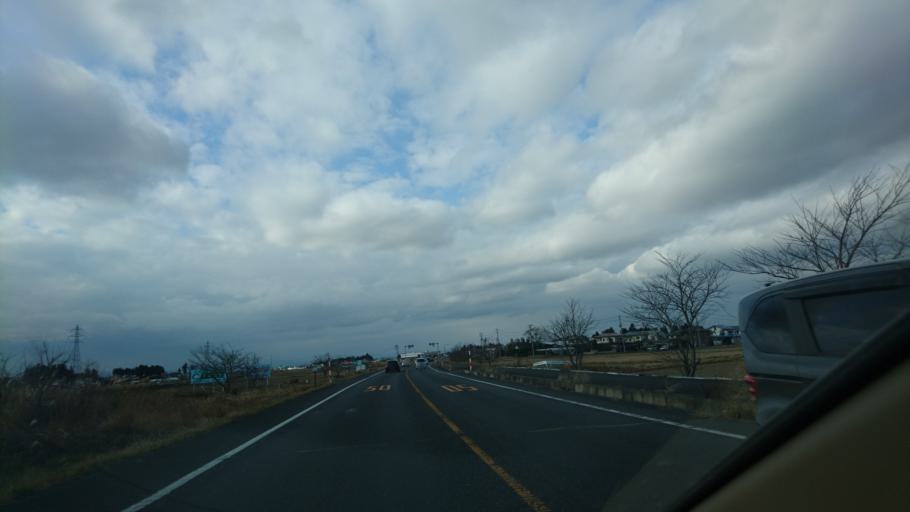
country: JP
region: Miyagi
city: Kogota
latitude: 38.5550
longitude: 141.0429
